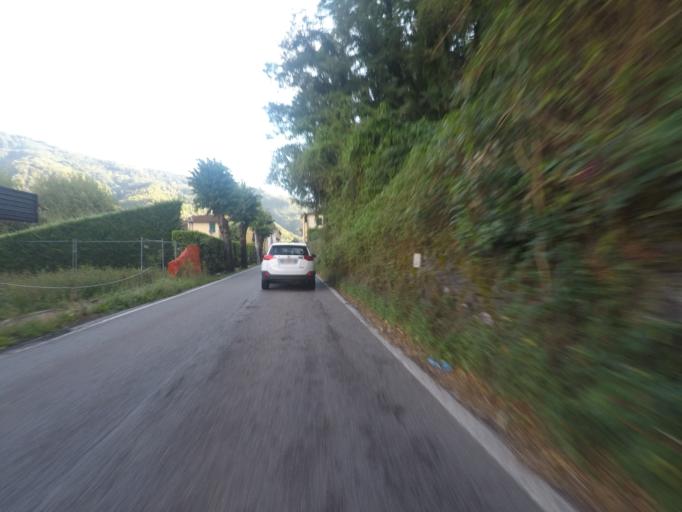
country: IT
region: Tuscany
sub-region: Provincia di Lucca
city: Bagni di Lucca
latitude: 44.0033
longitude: 10.5616
